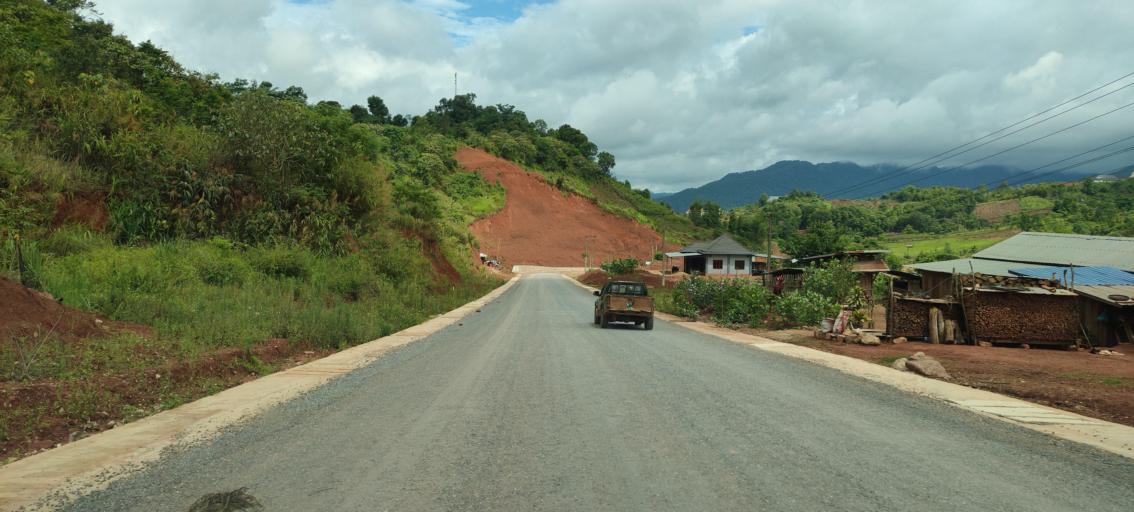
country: LA
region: Phongsali
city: Phongsali
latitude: 21.6348
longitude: 101.9215
